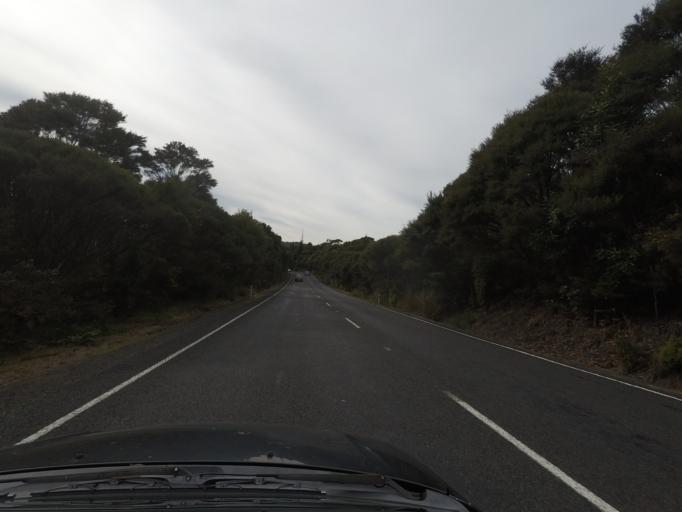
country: NZ
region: Auckland
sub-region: Auckland
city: Titirangi
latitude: -36.9411
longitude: 174.5534
